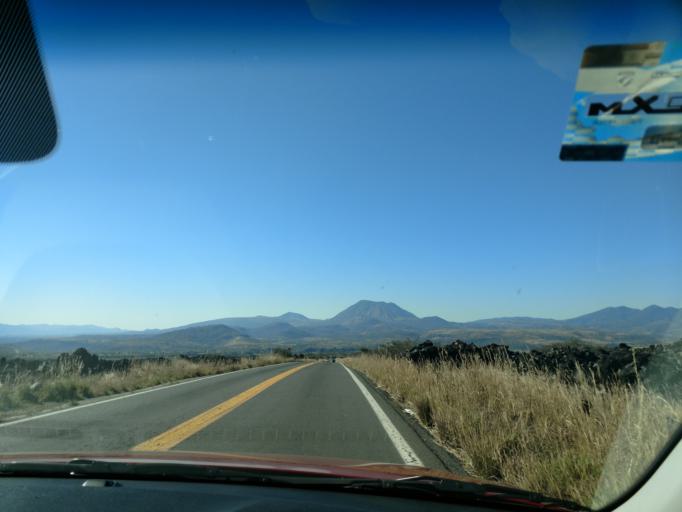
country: MX
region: Nayarit
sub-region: Ahuacatlan
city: Ahuacatlan
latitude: 21.0918
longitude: -104.5733
